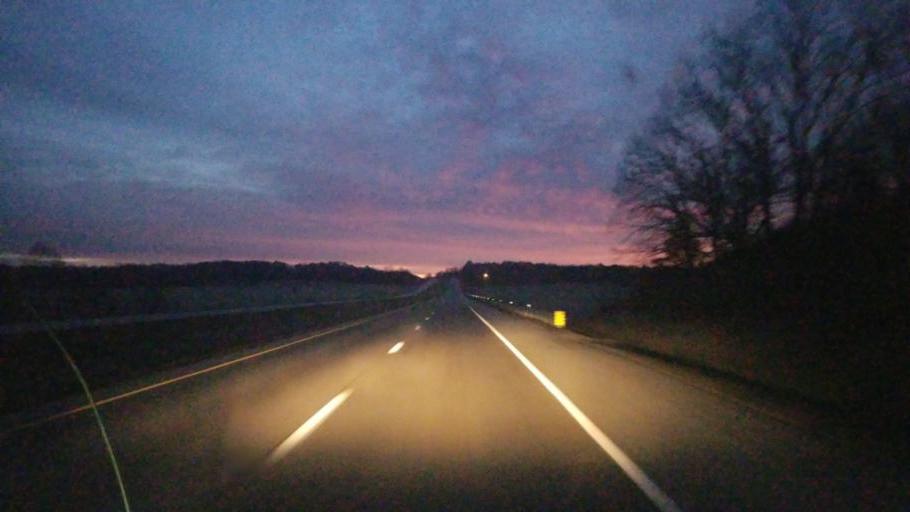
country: US
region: Missouri
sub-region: Howell County
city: Mountain View
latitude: 36.9893
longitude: -91.5329
